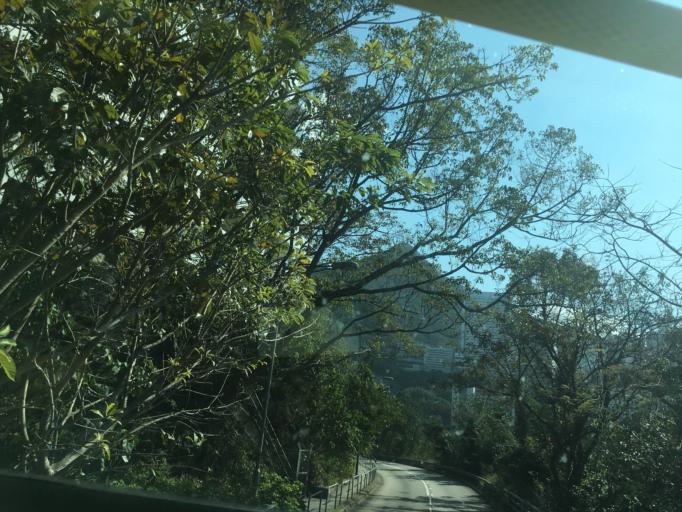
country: HK
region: Central and Western
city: Central
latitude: 22.2723
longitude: 114.1228
